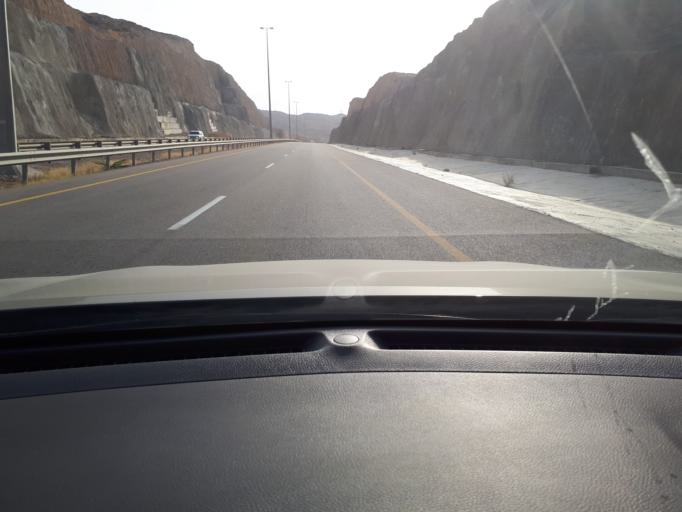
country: OM
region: Muhafazat Masqat
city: Muscat
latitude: 23.2062
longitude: 58.9097
